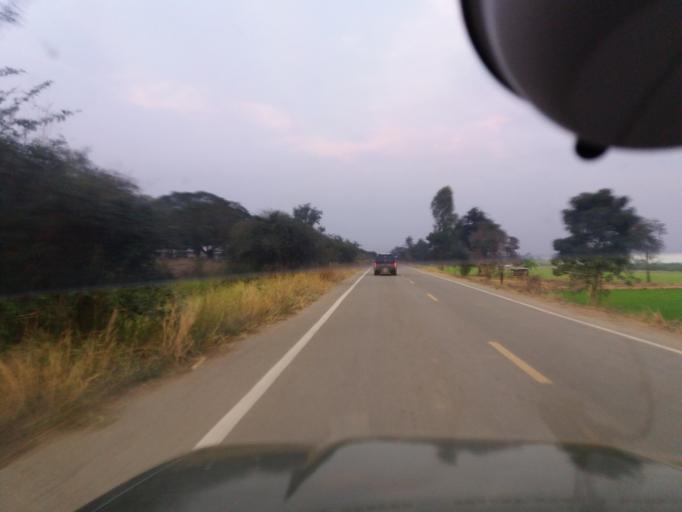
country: TH
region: Suphan Buri
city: Doem Bang Nang Buat
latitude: 14.9001
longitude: 100.1334
